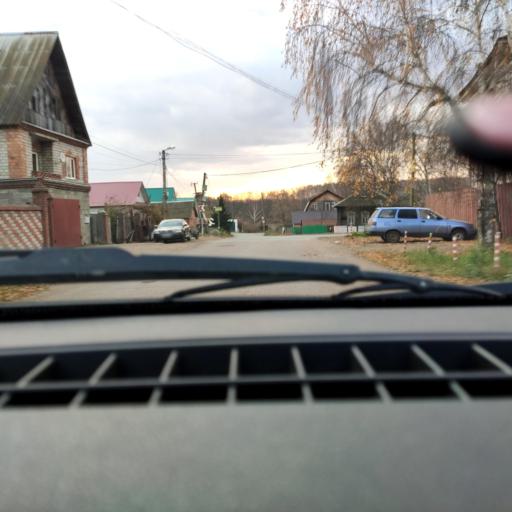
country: RU
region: Bashkortostan
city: Iglino
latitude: 54.8335
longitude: 56.1929
